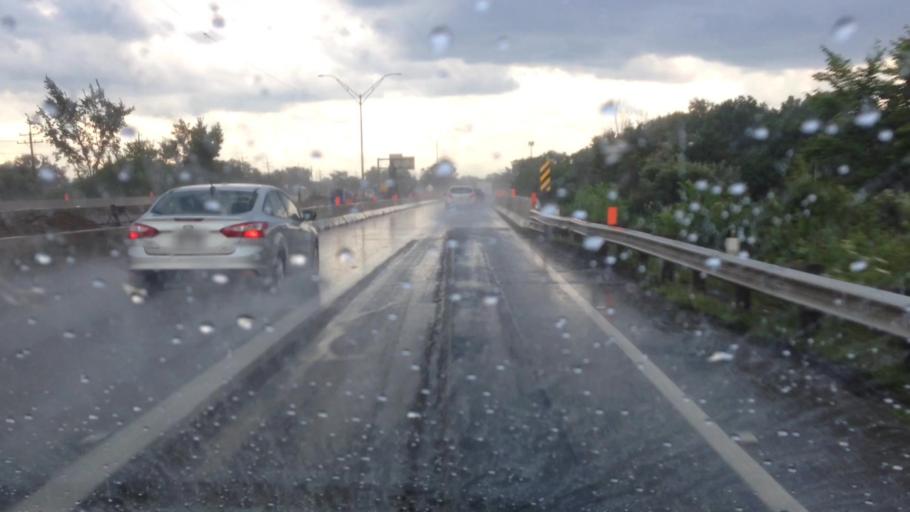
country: US
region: Ohio
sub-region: Cuyahoga County
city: Bedford Heights
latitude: 41.4180
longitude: -81.5178
